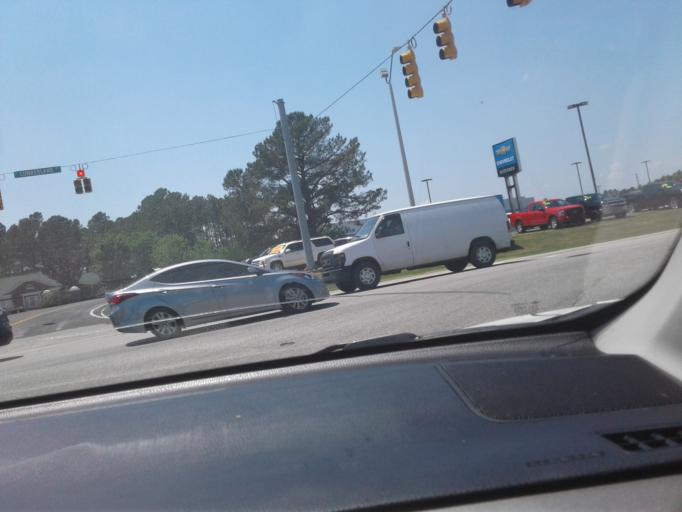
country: US
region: North Carolina
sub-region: Harnett County
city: Dunn
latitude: 35.2928
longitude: -78.5962
